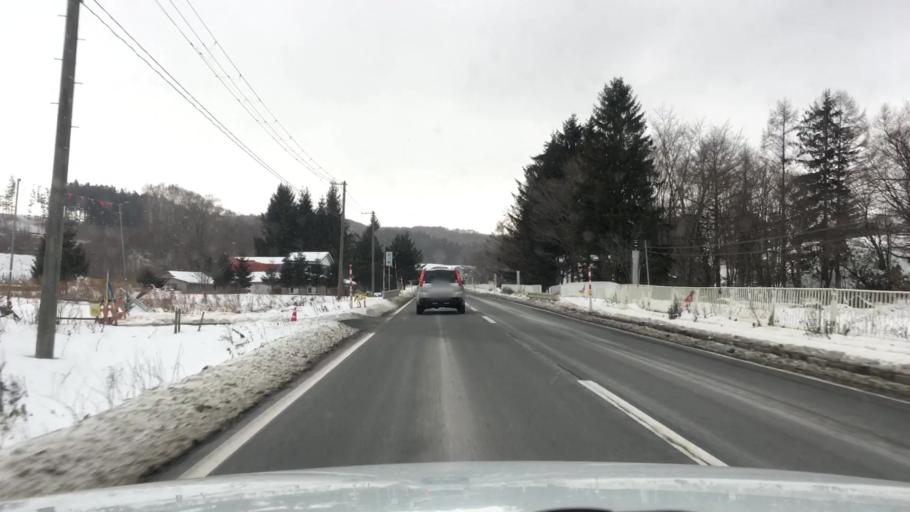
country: JP
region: Iwate
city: Morioka-shi
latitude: 39.6468
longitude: 141.3623
